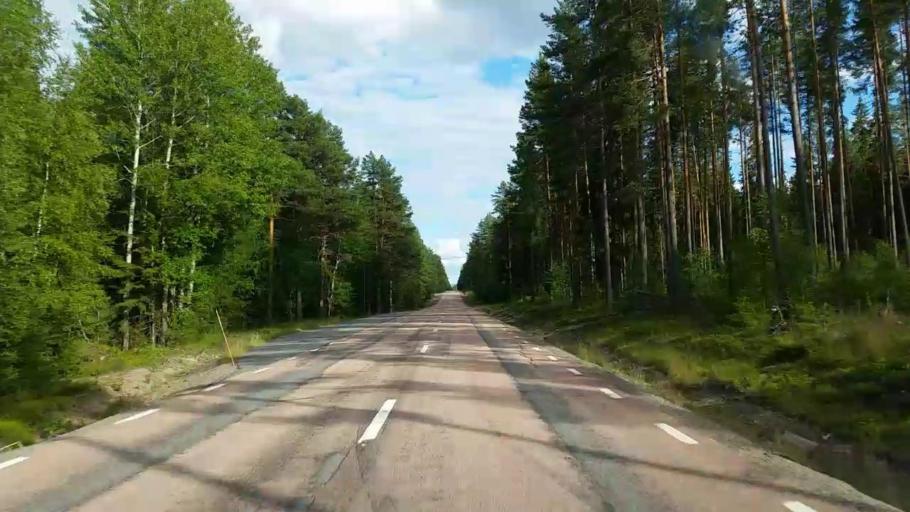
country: SE
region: Gaevleborg
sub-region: Ljusdals Kommun
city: Farila
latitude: 61.8869
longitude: 15.9291
